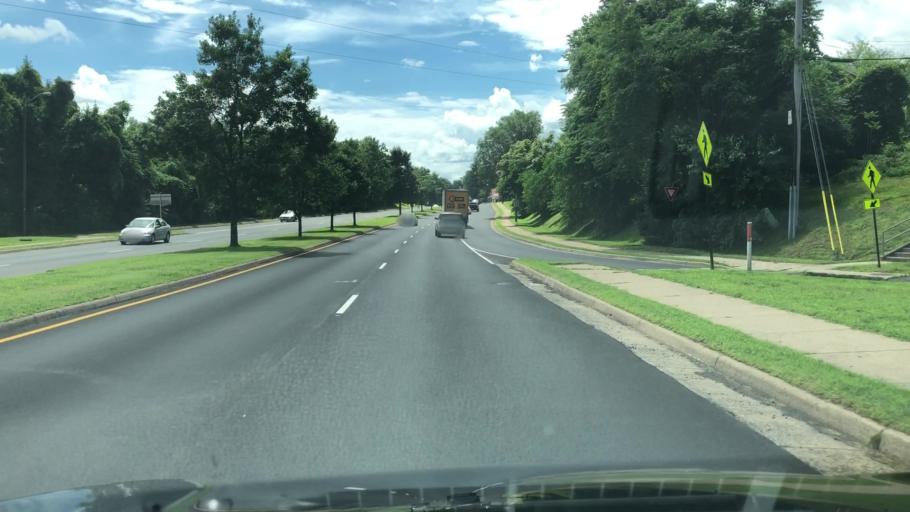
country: US
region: Virginia
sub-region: City of Fredericksburg
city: Fredericksburg
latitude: 38.2896
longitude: -77.4566
